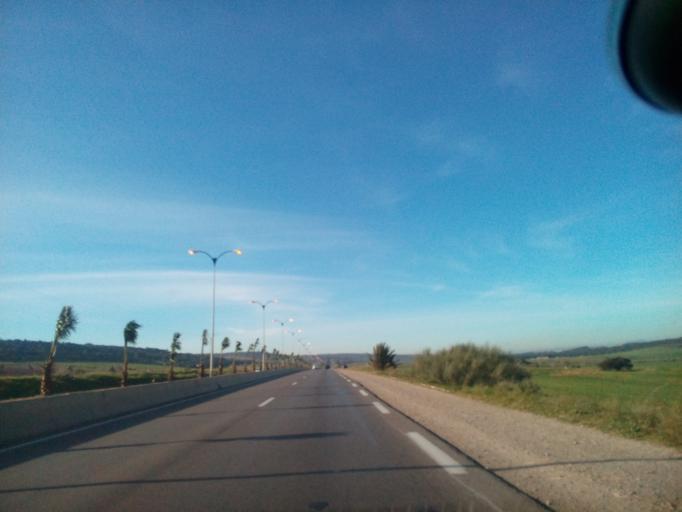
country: DZ
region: Mostaganem
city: Mostaganem
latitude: 35.8190
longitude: -0.0211
